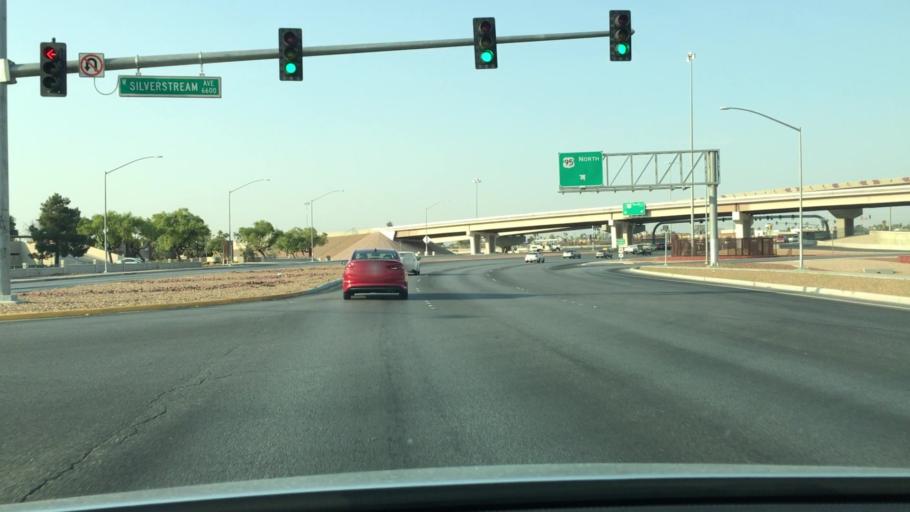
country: US
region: Nevada
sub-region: Clark County
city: Spring Valley
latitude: 36.1789
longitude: -115.2424
